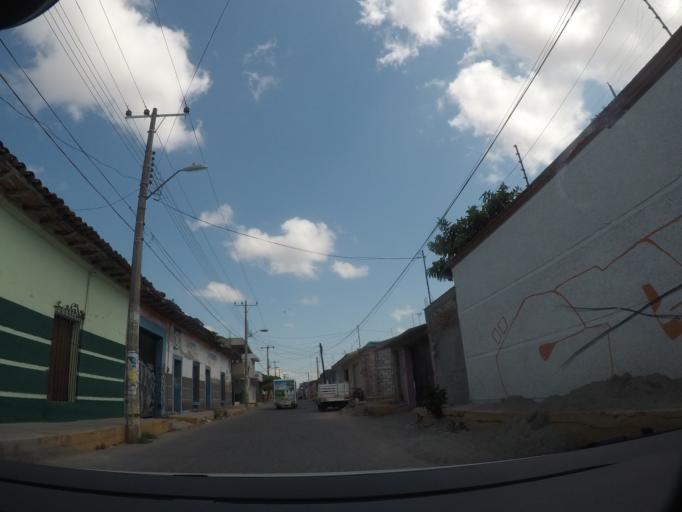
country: MX
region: Oaxaca
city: Juchitan de Zaragoza
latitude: 16.4383
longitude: -95.0209
